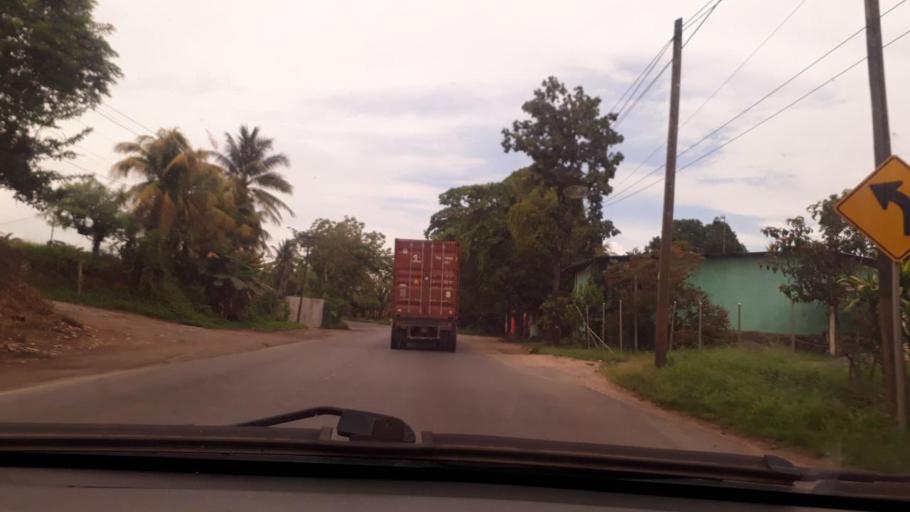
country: GT
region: Izabal
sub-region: Municipio de Puerto Barrios
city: Puerto Barrios
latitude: 15.5915
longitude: -88.5748
